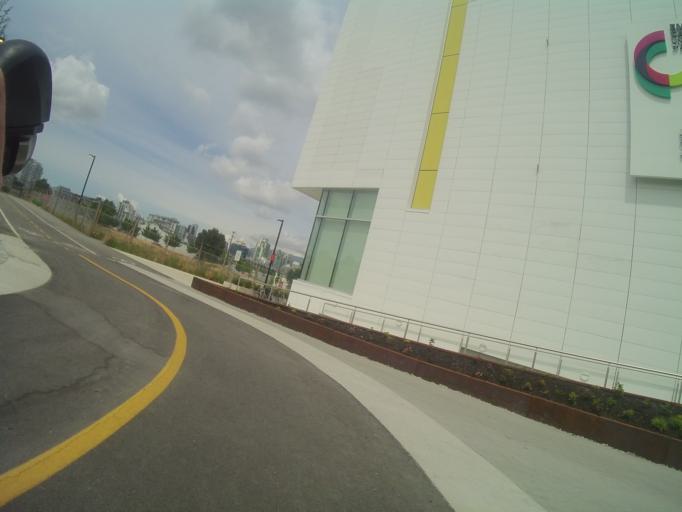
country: CA
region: British Columbia
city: Vancouver
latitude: 49.2673
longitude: -123.0933
